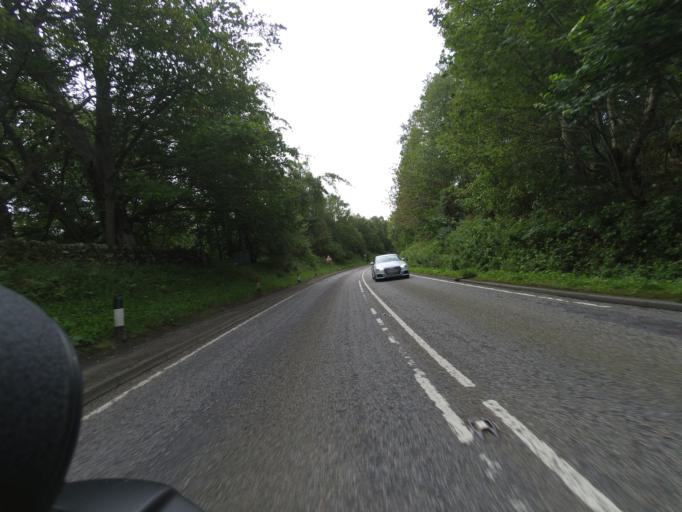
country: GB
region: Scotland
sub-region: Highland
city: Golspie
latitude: 57.9797
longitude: -3.9583
